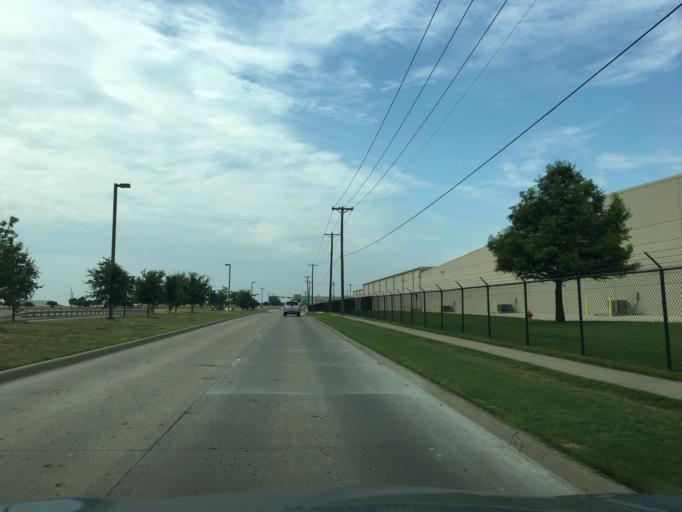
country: US
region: Texas
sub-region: Collin County
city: McKinney
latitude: 33.1807
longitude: -96.5984
